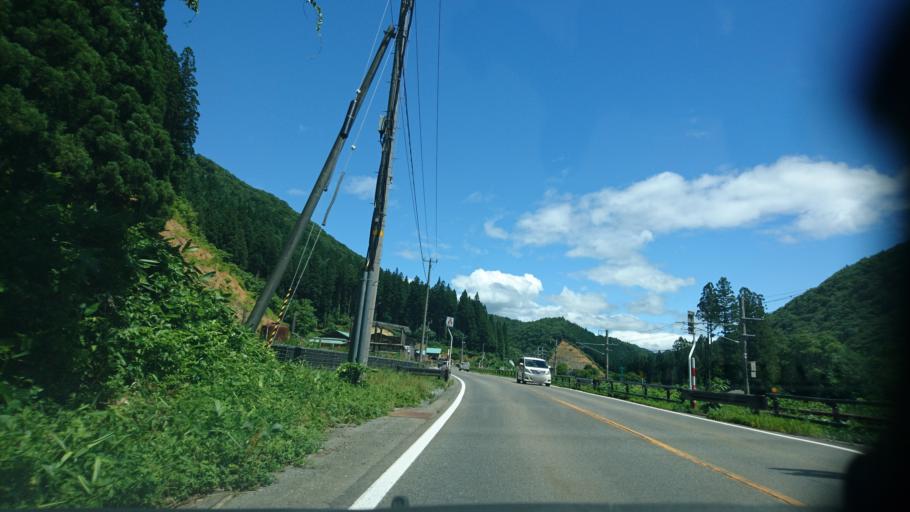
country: JP
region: Akita
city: Kakunodatemachi
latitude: 39.6458
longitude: 140.6643
